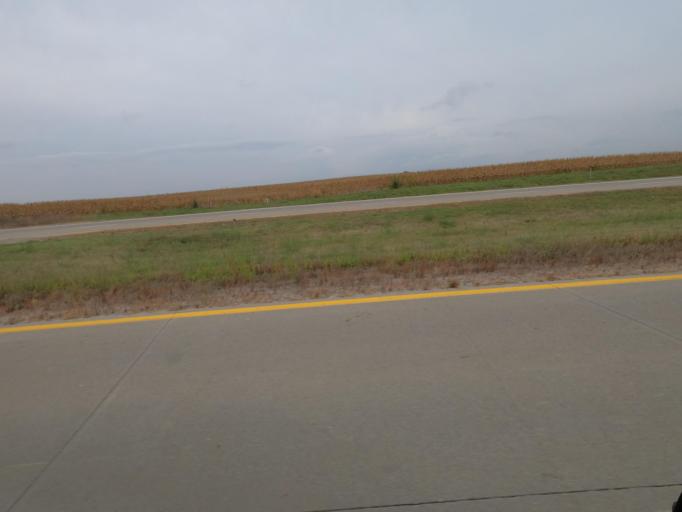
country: US
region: Iowa
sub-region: Mahaska County
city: Oskaloosa
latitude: 41.3538
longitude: -92.7616
